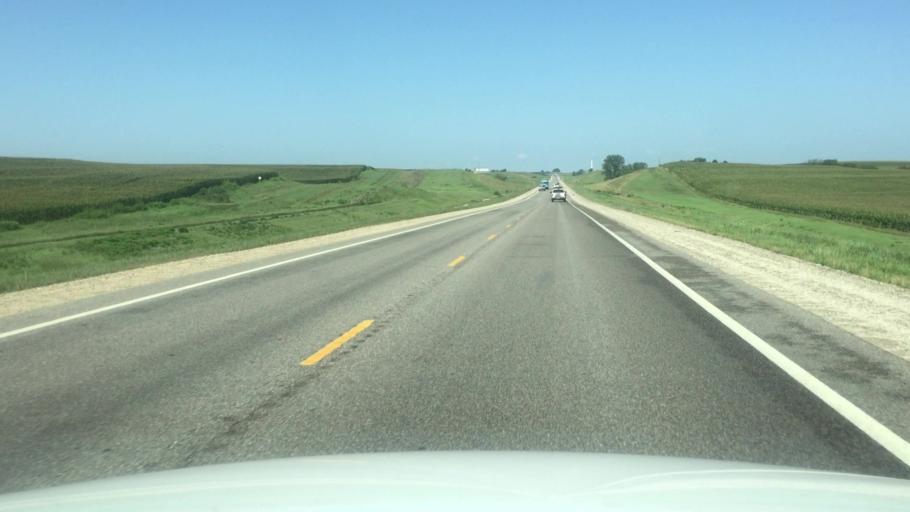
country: US
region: Kansas
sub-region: Doniphan County
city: Highland
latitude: 39.8422
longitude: -95.3078
